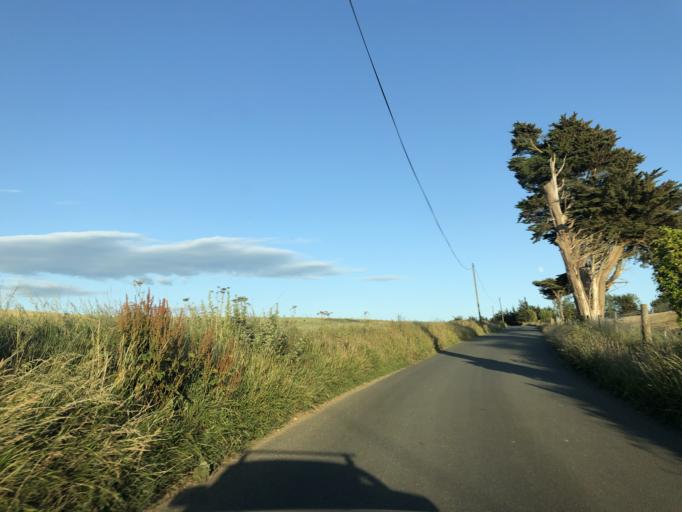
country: GB
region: England
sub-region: Isle of Wight
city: Chale
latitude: 50.6368
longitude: -1.3351
